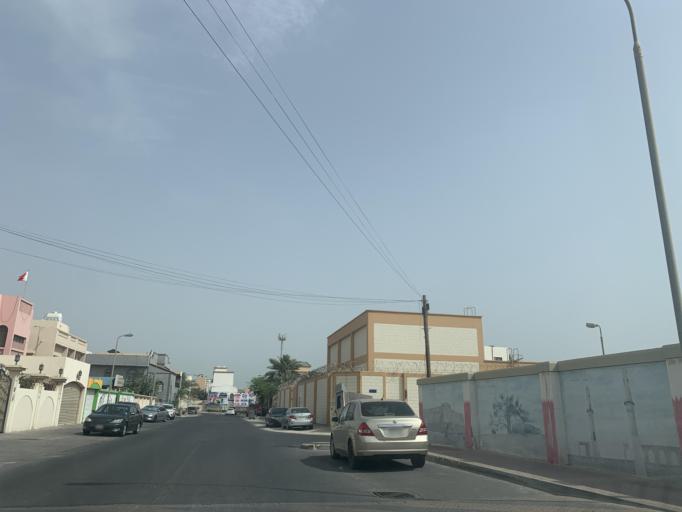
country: BH
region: Northern
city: Ar Rifa'
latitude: 26.1305
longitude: 50.5699
